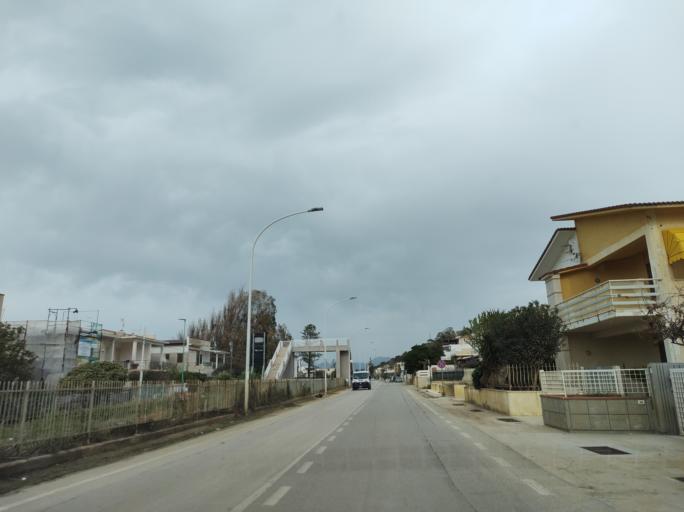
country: IT
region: Sicily
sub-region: Trapani
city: Alcamo
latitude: 38.0261
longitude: 12.9271
